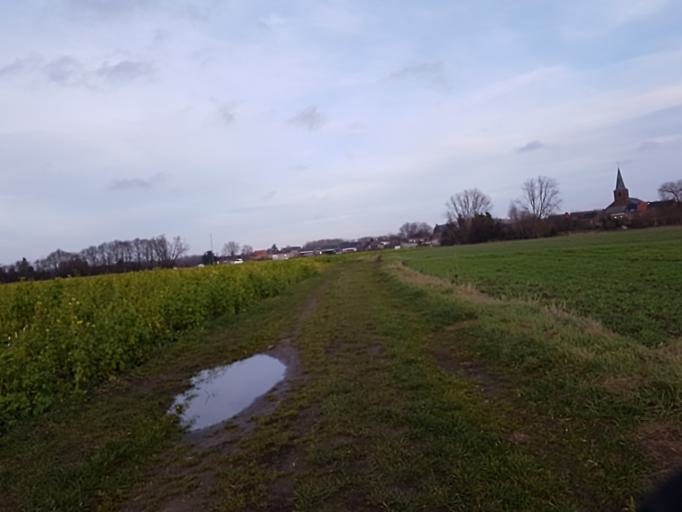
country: BE
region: Flanders
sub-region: Provincie Vlaams-Brabant
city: Rotselaar
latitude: 50.9497
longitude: 4.7049
